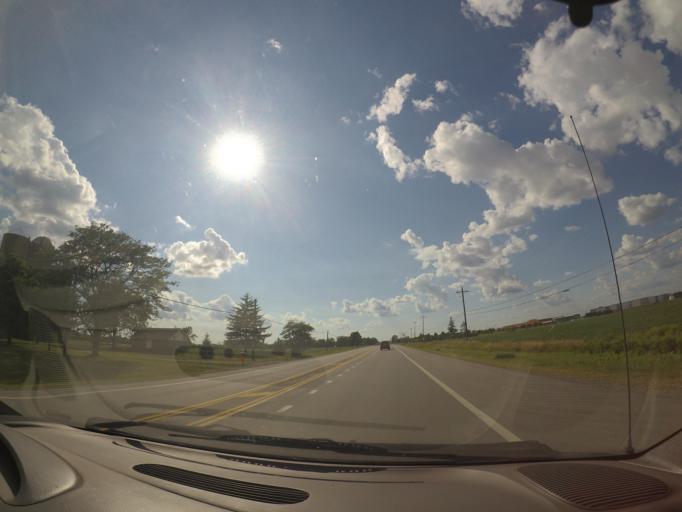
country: US
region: Ohio
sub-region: Wood County
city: Perrysburg
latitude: 41.5382
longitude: -83.5742
